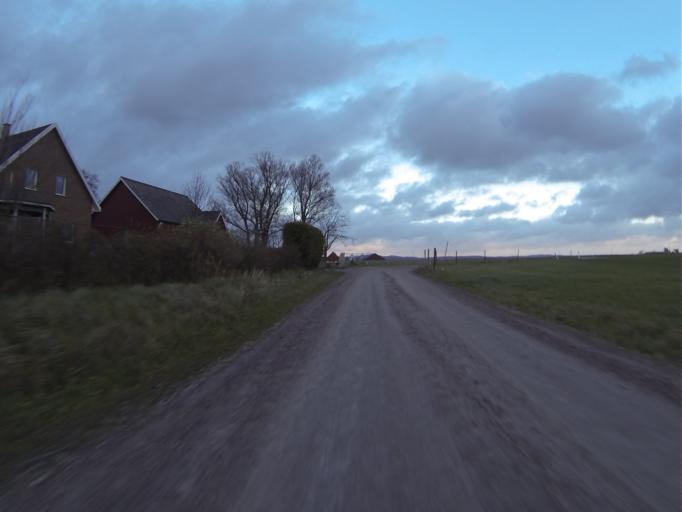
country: SE
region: Skane
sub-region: Lunds Kommun
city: Genarp
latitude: 55.6231
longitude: 13.3398
